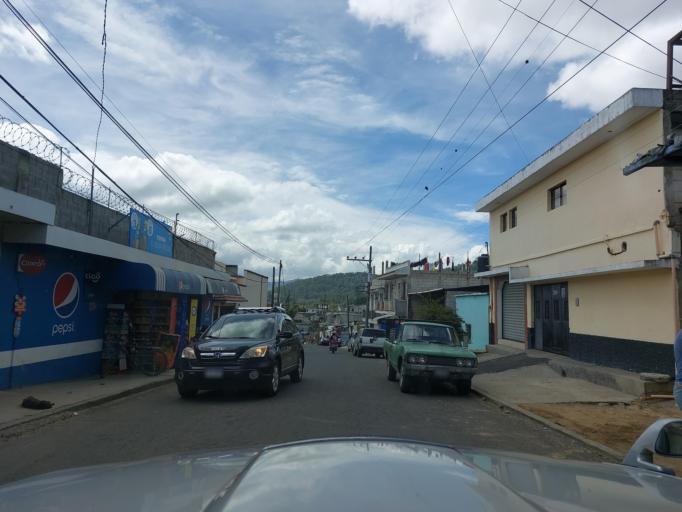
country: GT
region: Chimaltenango
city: San Andres Itzapa
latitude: 14.6216
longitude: -90.8381
